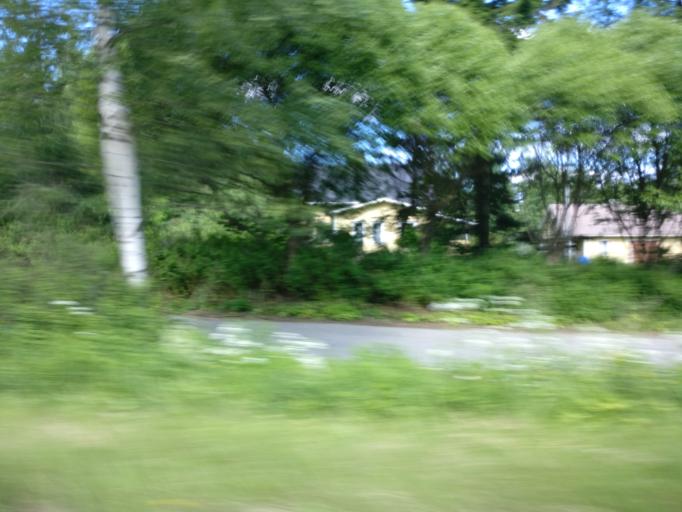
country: FI
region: Southern Savonia
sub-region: Savonlinna
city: Kerimaeki
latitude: 61.8217
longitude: 29.2517
